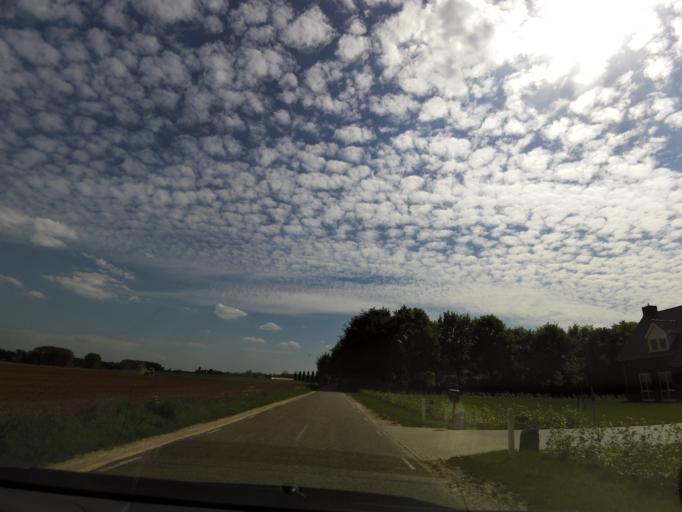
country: NL
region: Limburg
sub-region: Gemeente Roerdalen
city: Sint Odilienberg
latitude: 51.1599
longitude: 5.9919
